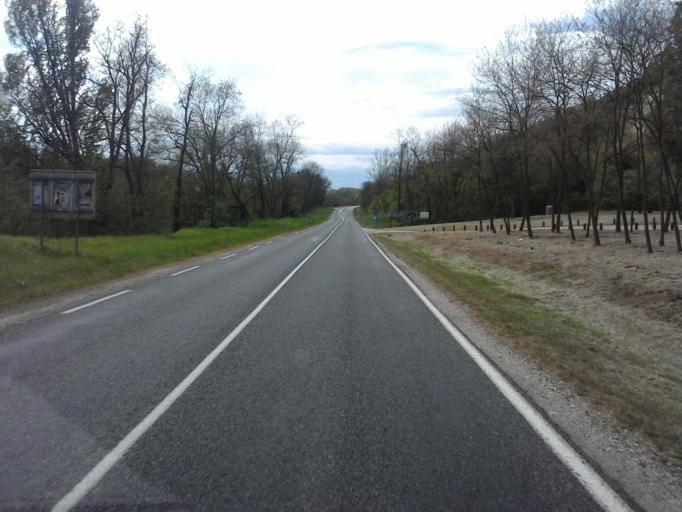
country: FR
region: Bourgogne
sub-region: Departement de l'Yonne
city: Vermenton
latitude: 47.6677
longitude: 3.7191
